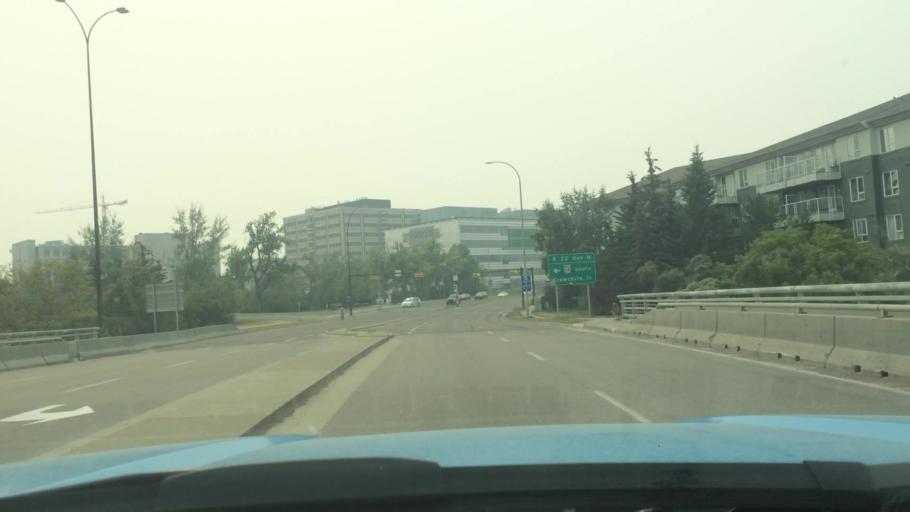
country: CA
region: Alberta
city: Calgary
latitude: 51.0831
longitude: -114.1258
